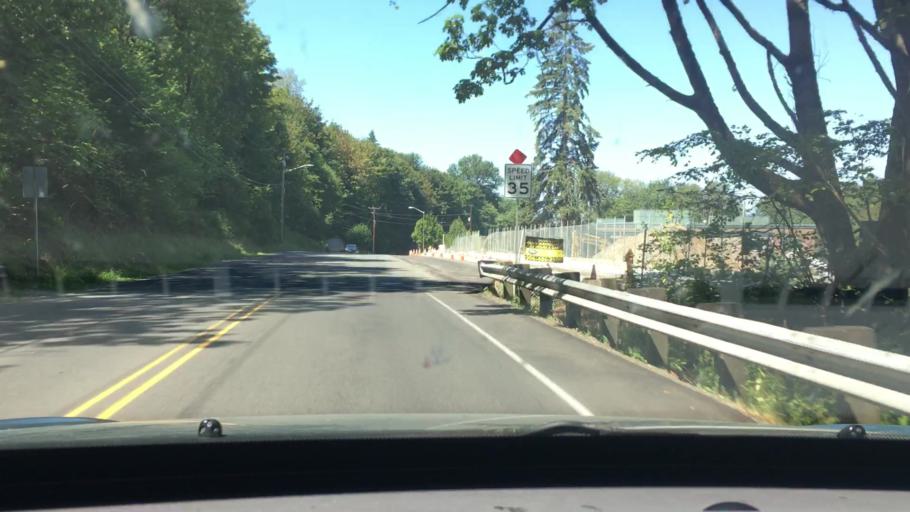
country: US
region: Washington
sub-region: King County
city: Newcastle
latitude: 47.5406
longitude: -122.1534
